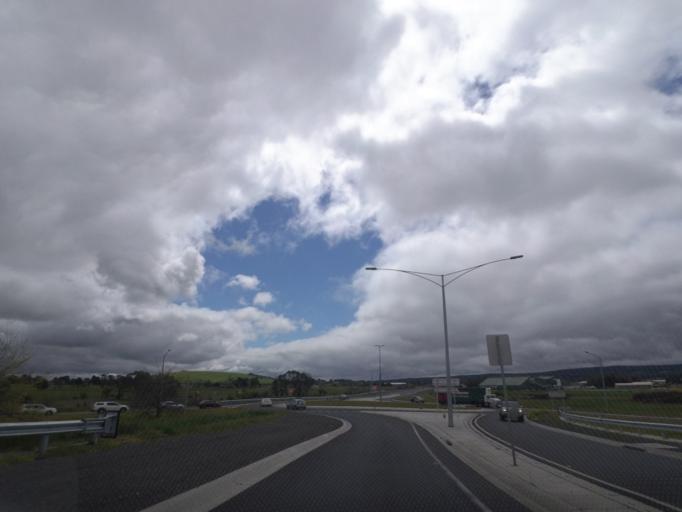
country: AU
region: Victoria
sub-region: Ballarat North
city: Lake Wendouree
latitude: -37.5190
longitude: 143.8442
